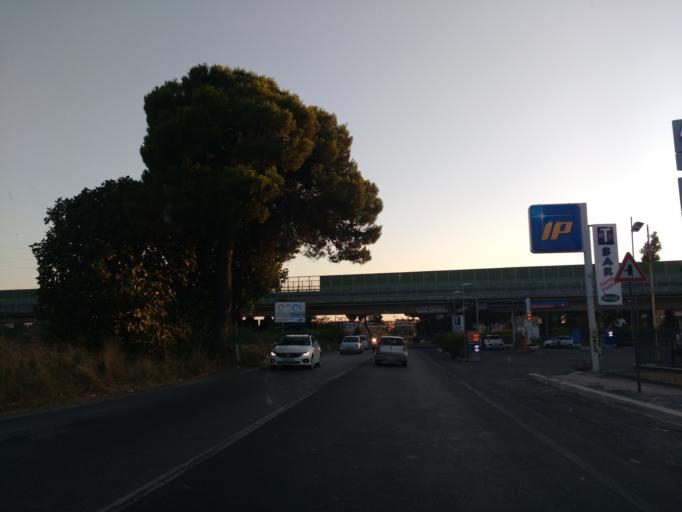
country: IT
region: Latium
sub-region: Citta metropolitana di Roma Capitale
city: Albuccione
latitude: 41.9536
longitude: 12.7030
